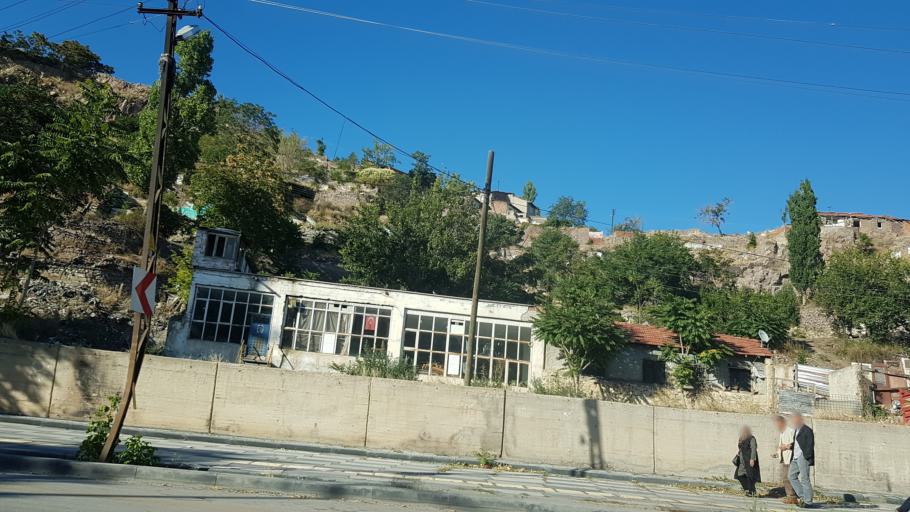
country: TR
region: Ankara
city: Cankaya
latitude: 39.9422
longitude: 32.8702
